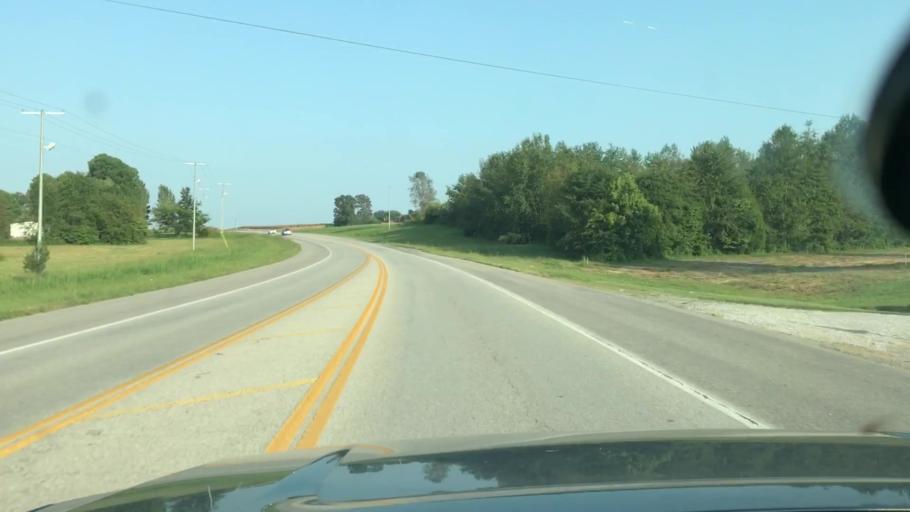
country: US
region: Tennessee
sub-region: Sumner County
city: Portland
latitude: 36.5850
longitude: -86.5842
